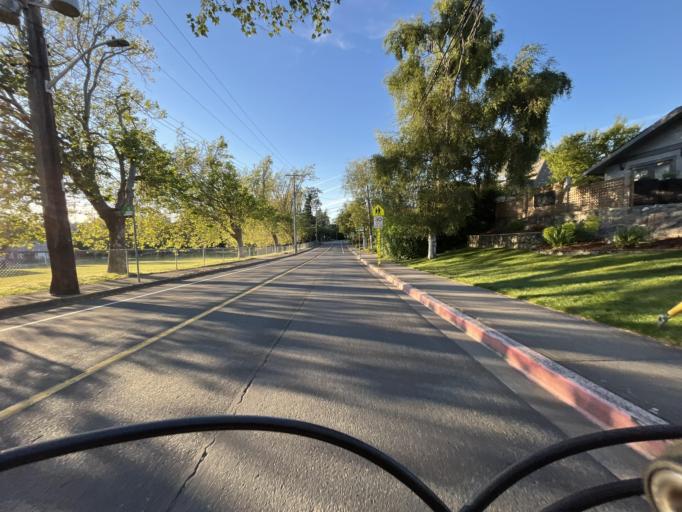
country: CA
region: British Columbia
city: Oak Bay
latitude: 48.4156
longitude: -123.3275
